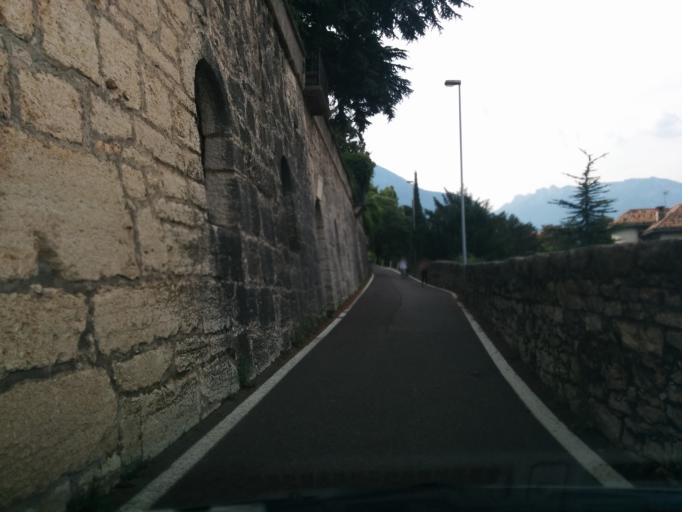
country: IT
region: Trentino-Alto Adige
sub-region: Provincia di Trento
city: Trento
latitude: 46.0723
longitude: 11.1301
